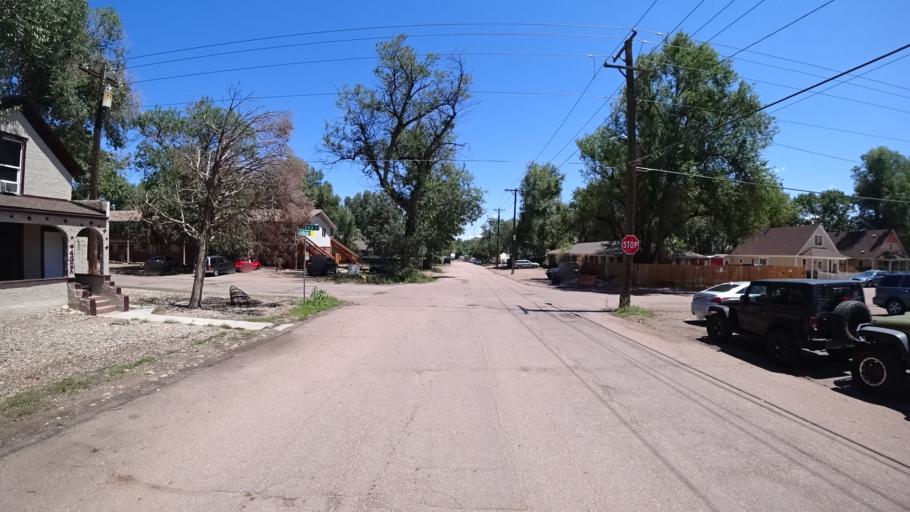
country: US
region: Colorado
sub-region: El Paso County
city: Colorado Springs
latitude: 38.8129
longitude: -104.8179
